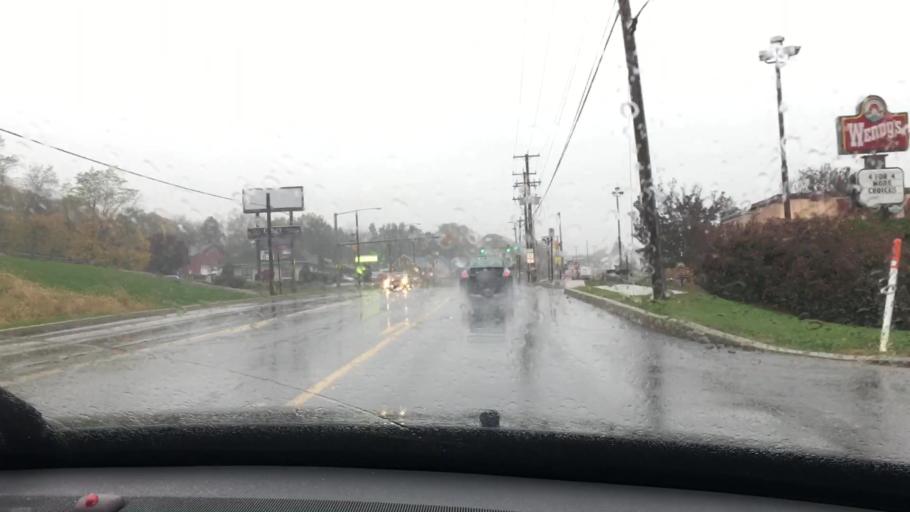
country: US
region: Pennsylvania
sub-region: York County
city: Shrewsbury
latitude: 39.7702
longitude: -76.6745
